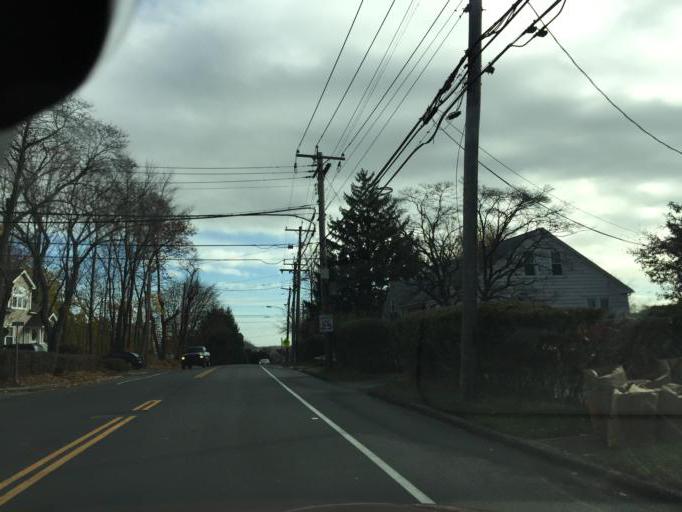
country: US
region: Connecticut
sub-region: Fairfield County
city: Bridgeport
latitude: 41.1744
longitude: -73.2379
